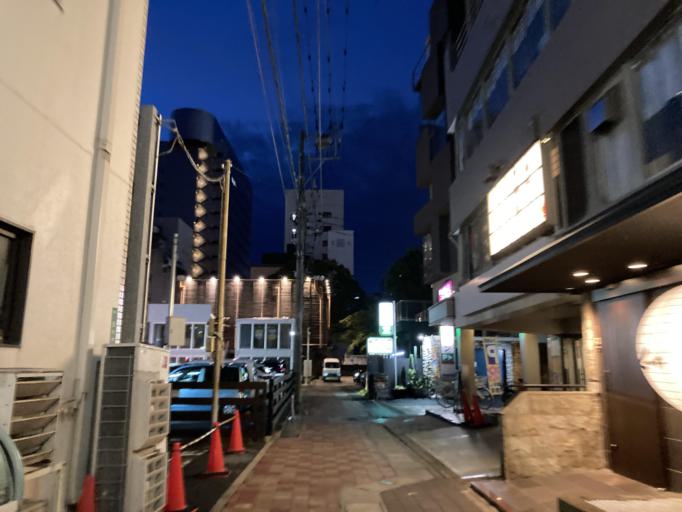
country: JP
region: Fukuoka
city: Fukuoka-shi
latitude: 33.5908
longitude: 130.4044
